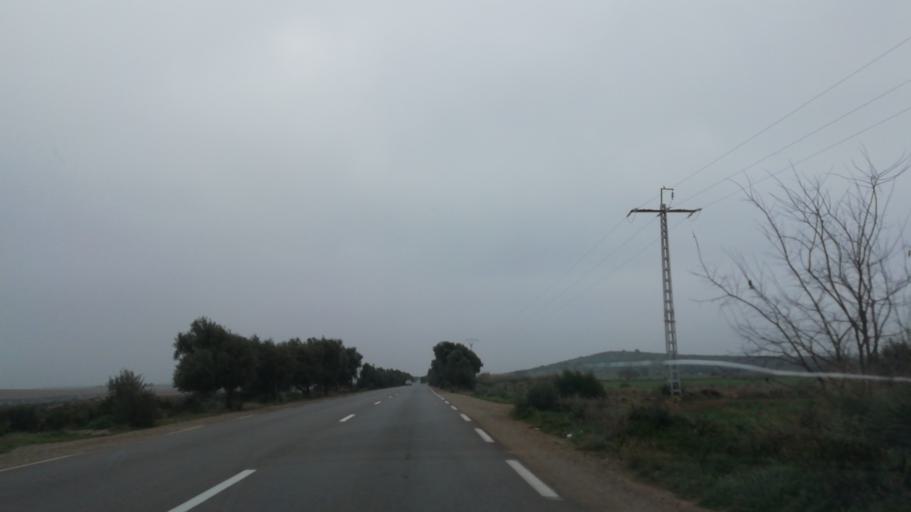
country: DZ
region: Mascara
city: Mascara
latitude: 35.3119
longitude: 0.3927
